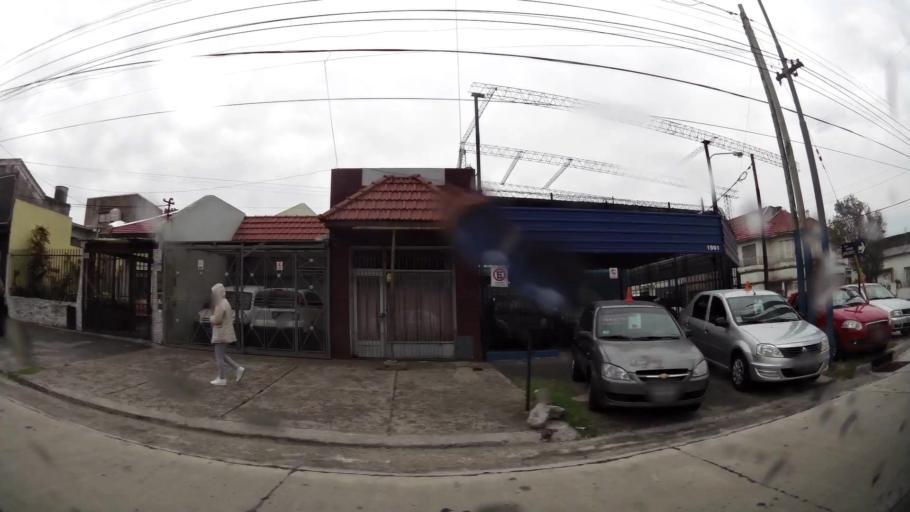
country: AR
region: Buenos Aires
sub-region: Partido de Lanus
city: Lanus
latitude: -34.6923
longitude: -58.4046
